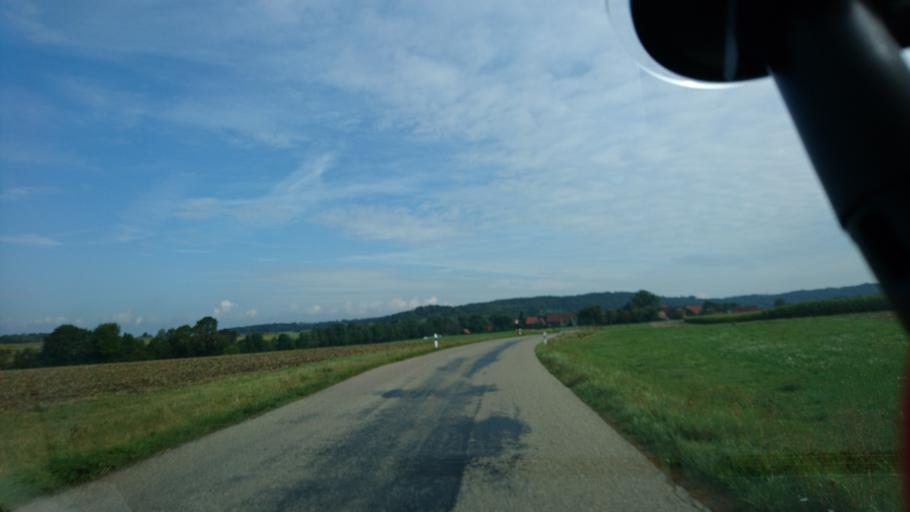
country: DE
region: Baden-Wuerttemberg
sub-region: Regierungsbezirk Stuttgart
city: Ilshofen
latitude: 49.1268
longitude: 9.9255
